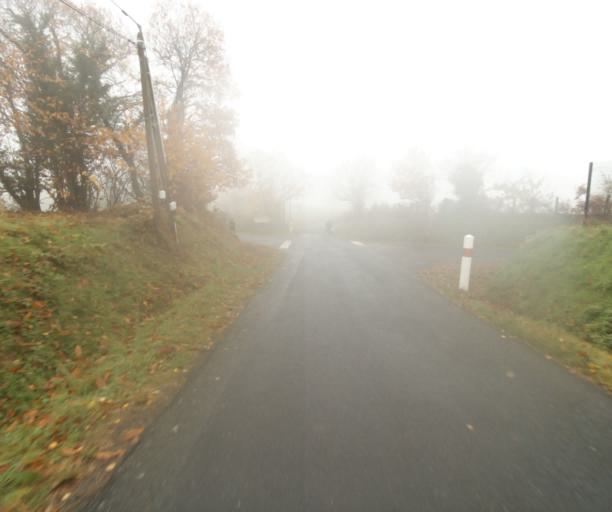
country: FR
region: Limousin
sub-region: Departement de la Correze
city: Sainte-Fereole
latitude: 45.1917
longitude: 1.6289
